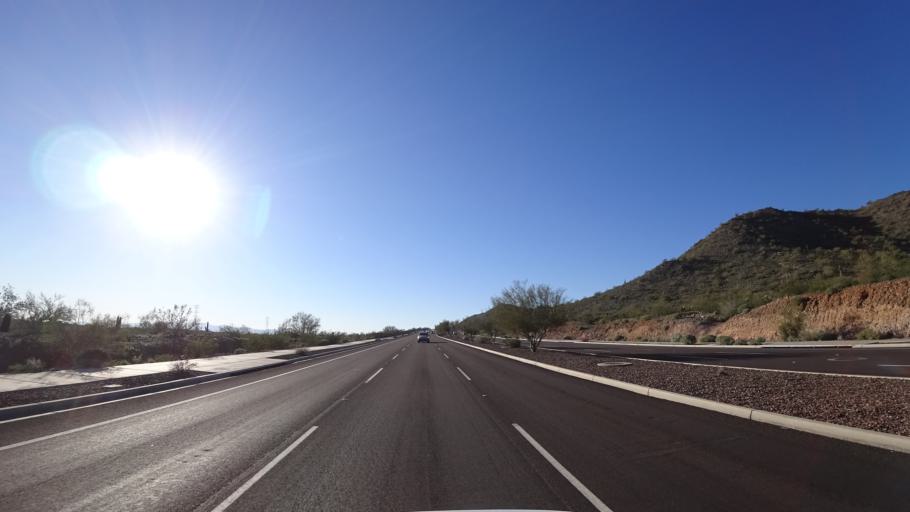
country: US
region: Arizona
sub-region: Maricopa County
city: Sun City West
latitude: 33.7097
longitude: -112.2384
